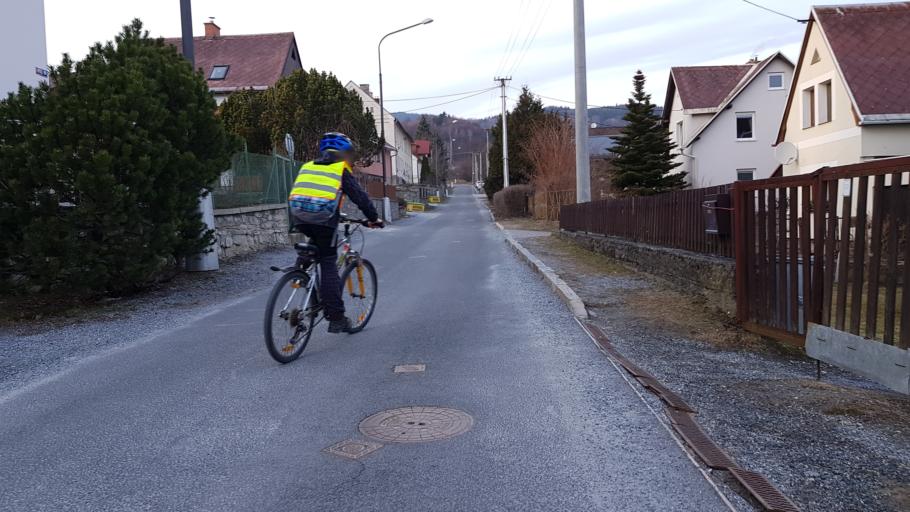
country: CZ
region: Olomoucky
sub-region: Okres Jesenik
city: Jesenik
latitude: 50.2281
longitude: 17.1876
